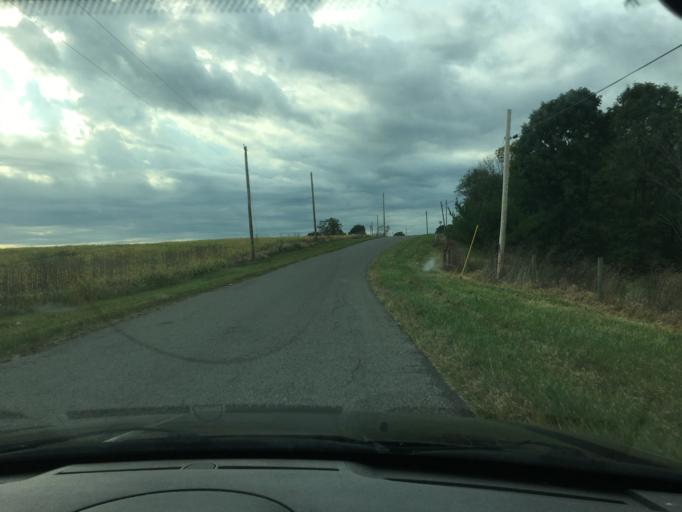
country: US
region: Ohio
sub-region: Logan County
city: Bellefontaine
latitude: 40.3341
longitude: -83.7978
